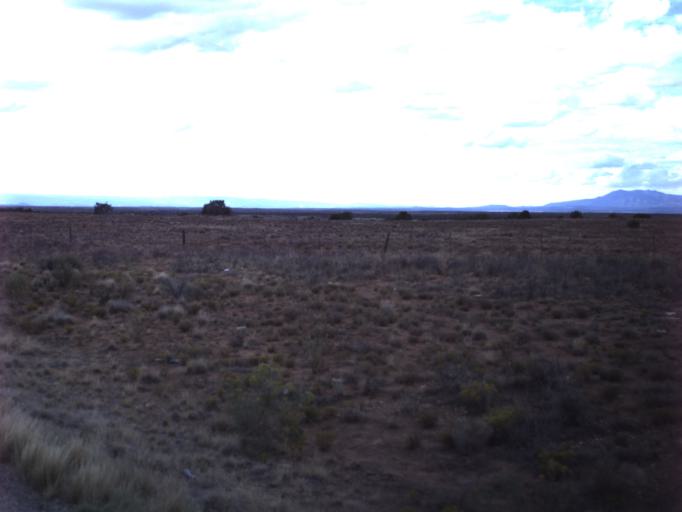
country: US
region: Utah
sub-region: San Juan County
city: Blanding
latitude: 37.4347
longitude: -109.3767
